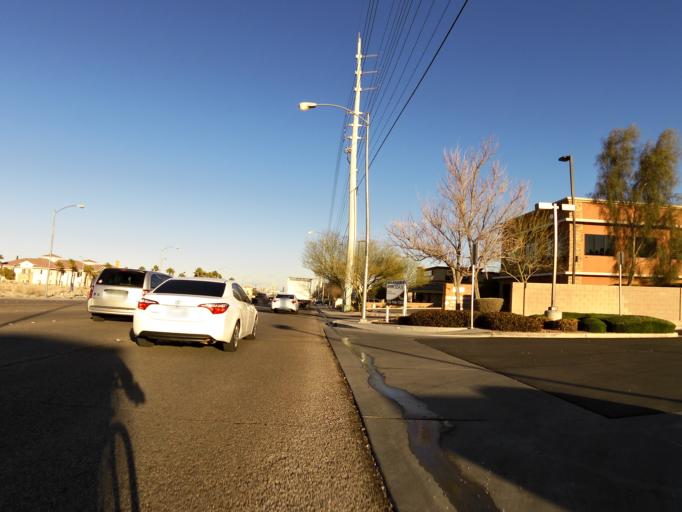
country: US
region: Nevada
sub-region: Clark County
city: Spring Valley
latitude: 36.1148
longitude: -115.2850
